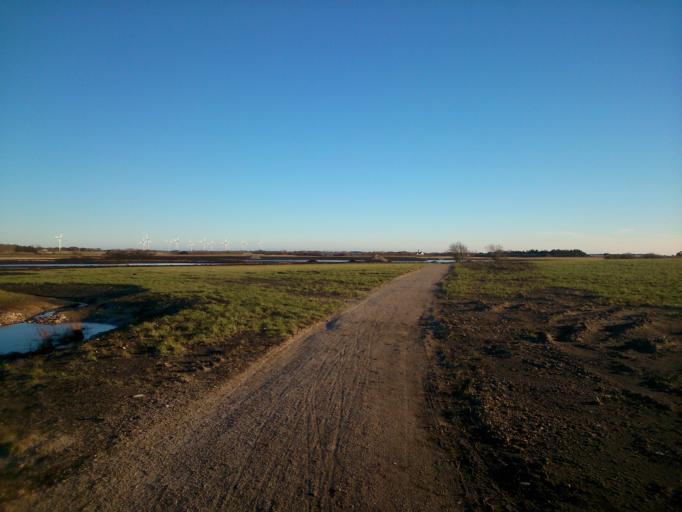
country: DK
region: Central Jutland
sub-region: Ringkobing-Skjern Kommune
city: Ringkobing
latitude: 56.0703
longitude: 8.2889
